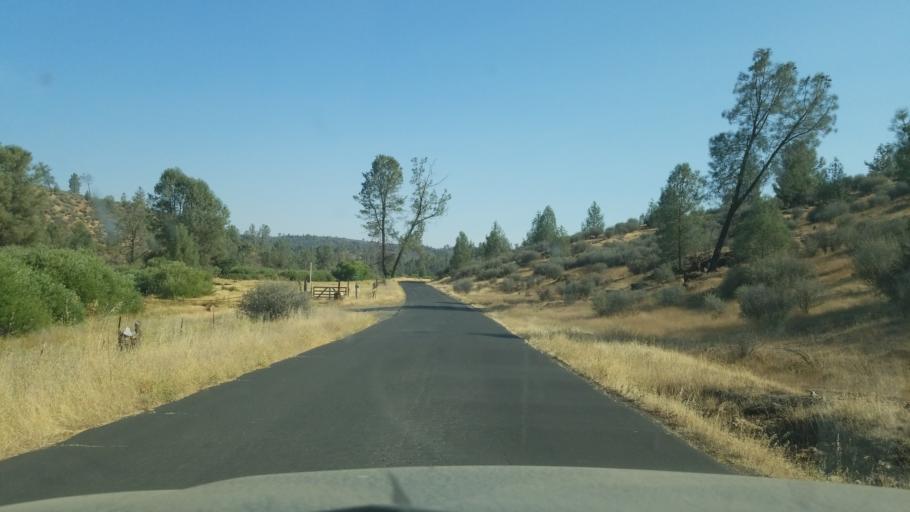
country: US
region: California
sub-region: Tuolumne County
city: Jamestown
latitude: 37.8534
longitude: -120.4535
